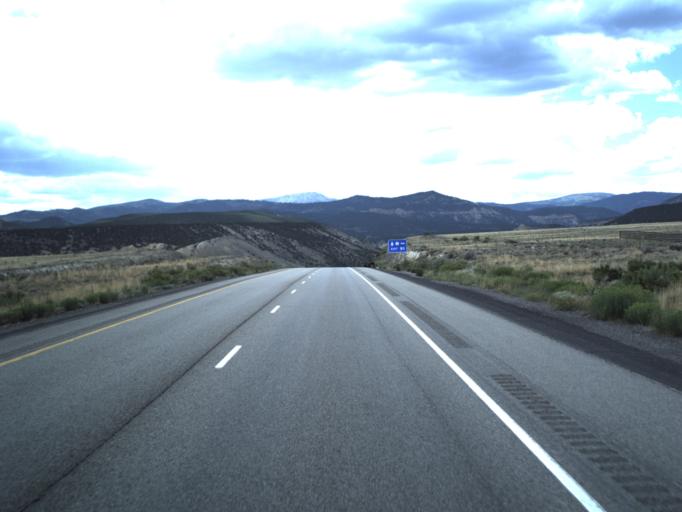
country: US
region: Utah
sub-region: Emery County
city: Ferron
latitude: 38.7709
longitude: -111.3356
